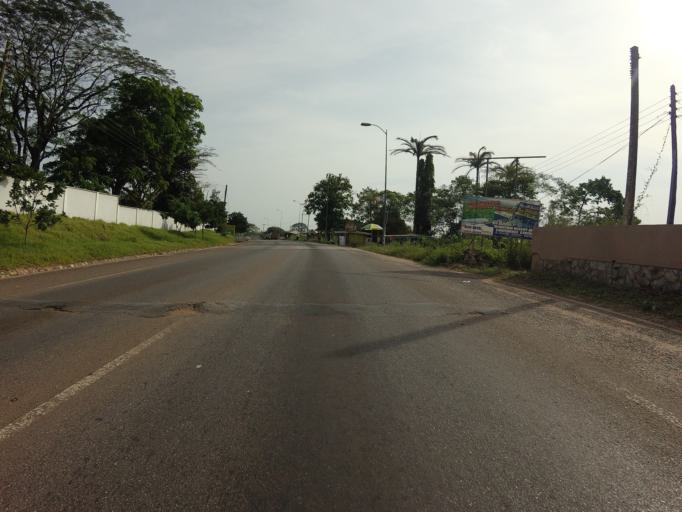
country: GH
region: Eastern
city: Aburi
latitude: 5.8356
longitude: -0.1798
